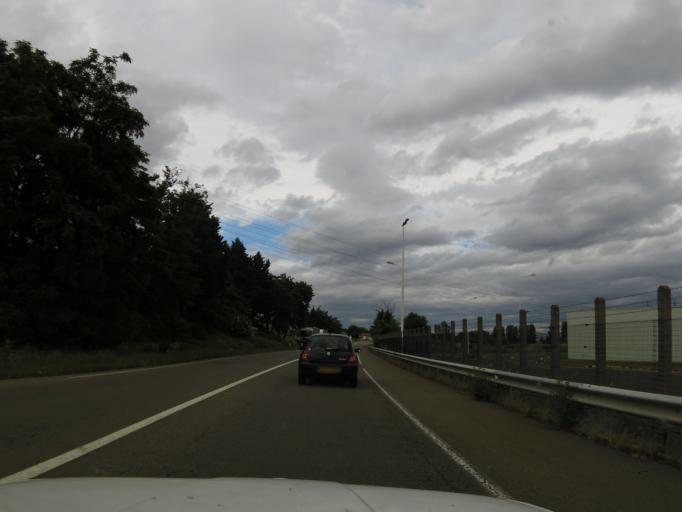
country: FR
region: Auvergne
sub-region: Departement du Puy-de-Dome
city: Gerzat
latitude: 45.8112
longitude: 3.1329
